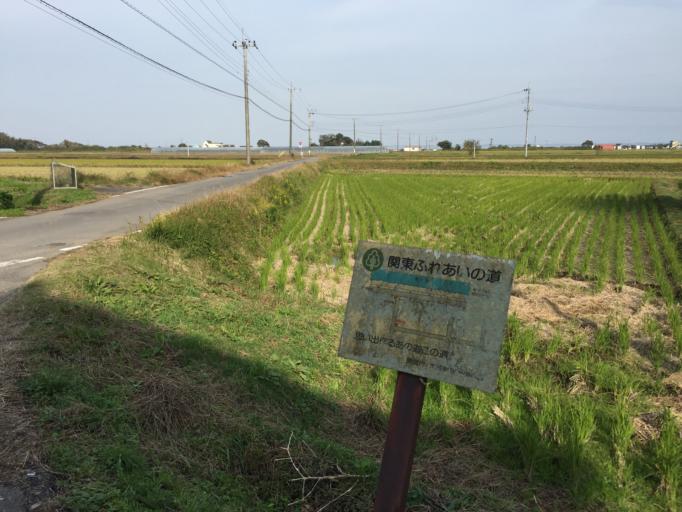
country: JP
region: Ibaraki
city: Inashiki
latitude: 36.0062
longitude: 140.3686
